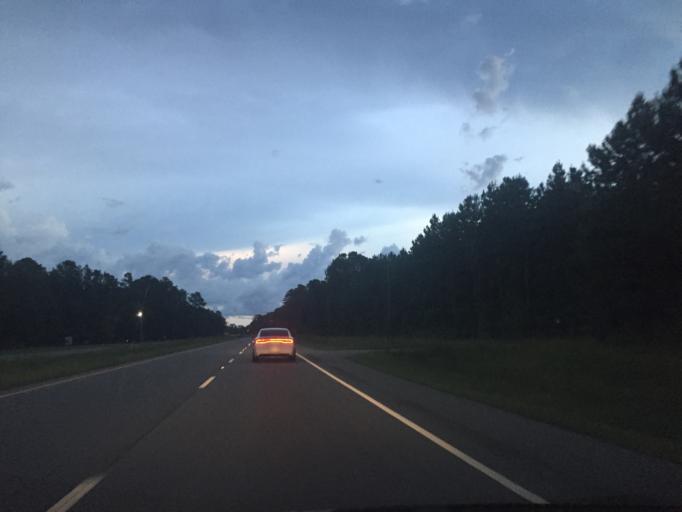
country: US
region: Georgia
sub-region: Liberty County
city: Midway
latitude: 31.8267
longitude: -81.5063
